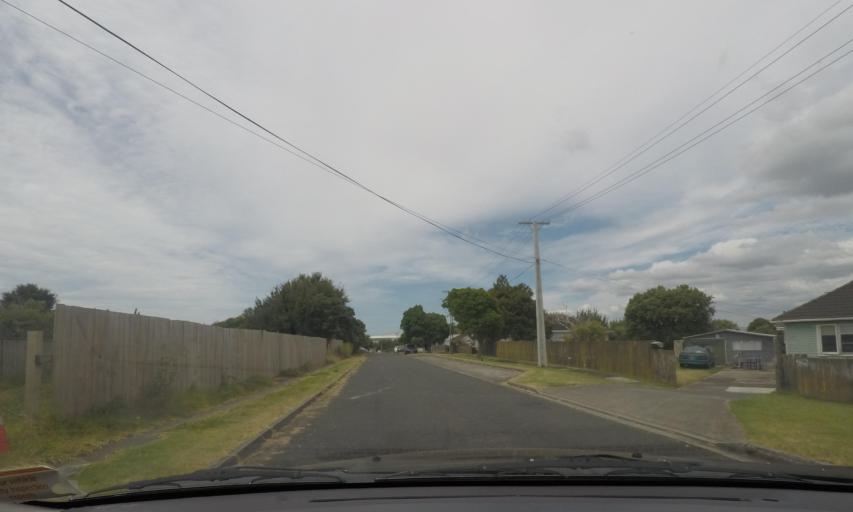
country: NZ
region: Auckland
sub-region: Auckland
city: Mangere
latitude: -36.9849
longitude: 174.7641
